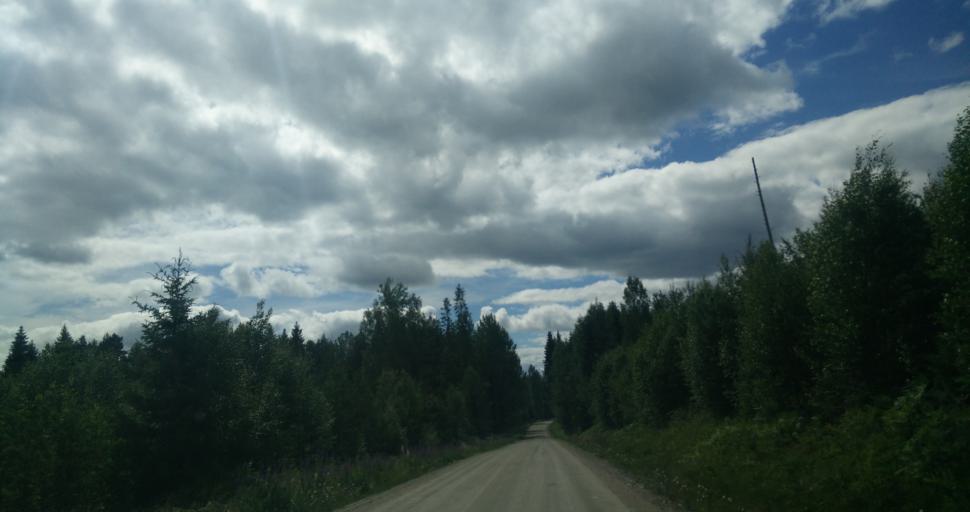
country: SE
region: Gaevleborg
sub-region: Nordanstigs Kommun
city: Bergsjoe
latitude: 62.1308
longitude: 17.1277
